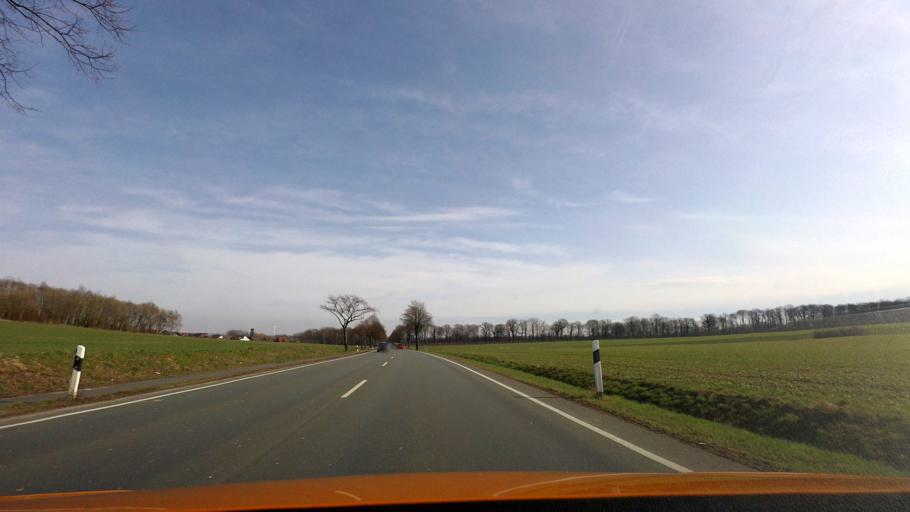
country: DE
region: Lower Saxony
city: Bad Nenndorf
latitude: 52.3301
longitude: 9.3923
